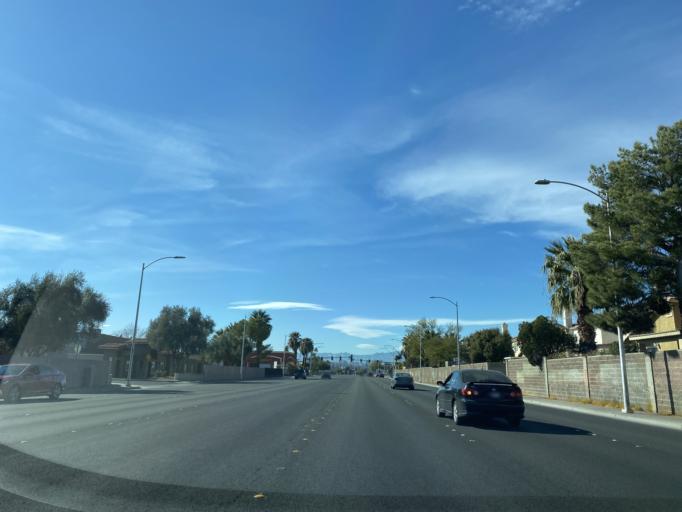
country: US
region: Nevada
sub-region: Clark County
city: Sunrise Manor
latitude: 36.1737
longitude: -115.0736
